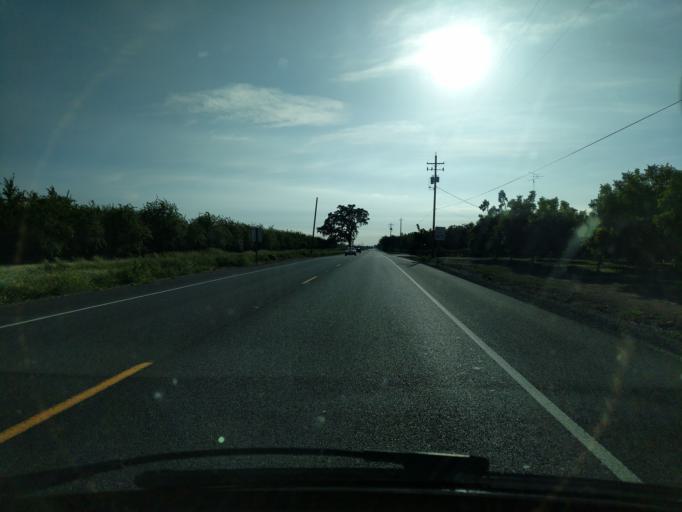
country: US
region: California
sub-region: San Joaquin County
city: Linden
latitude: 37.9300
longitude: -121.0053
